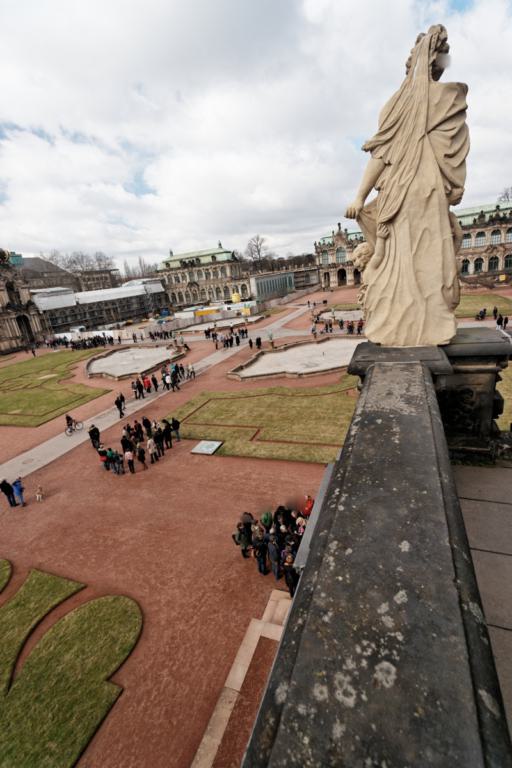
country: DE
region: Saxony
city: Dresden
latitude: 51.0526
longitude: 13.7346
